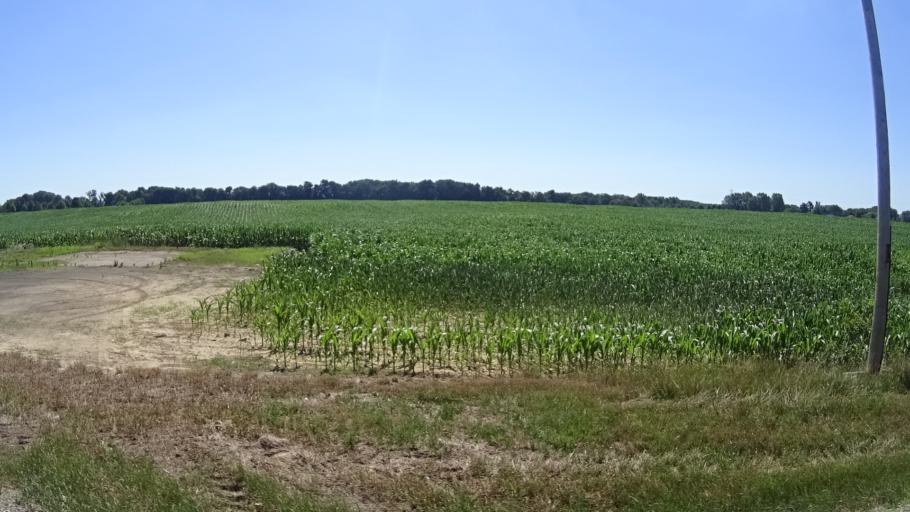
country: US
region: Ohio
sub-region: Erie County
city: Huron
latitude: 41.3634
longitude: -82.5727
